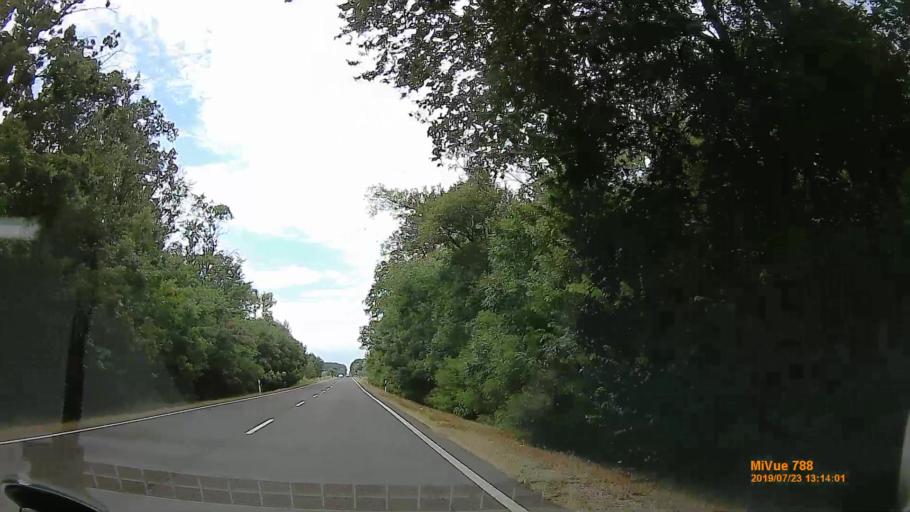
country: HU
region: Hajdu-Bihar
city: Gorbehaza
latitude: 47.9217
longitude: 21.2191
